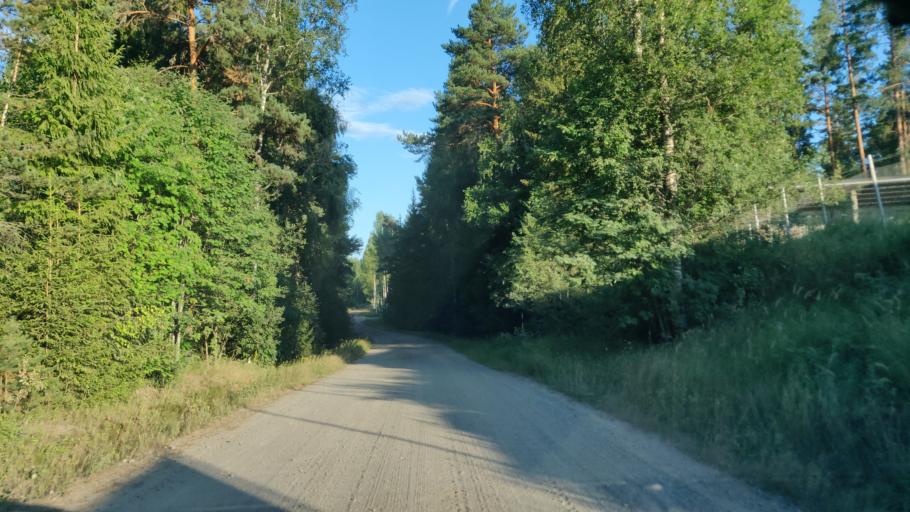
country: SE
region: Vaermland
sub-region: Hagfors Kommun
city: Ekshaerad
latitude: 60.1668
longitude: 13.5013
